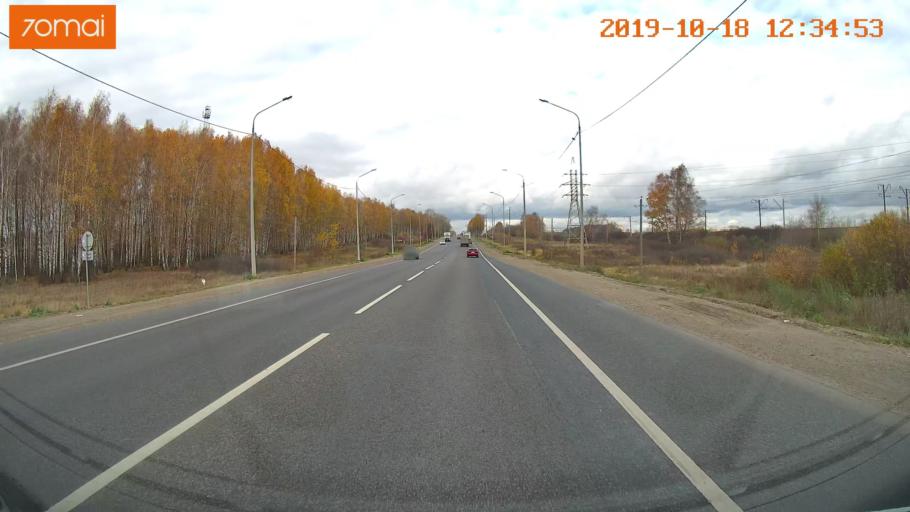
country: RU
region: Rjazan
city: Ryazan'
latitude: 54.6188
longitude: 39.6366
